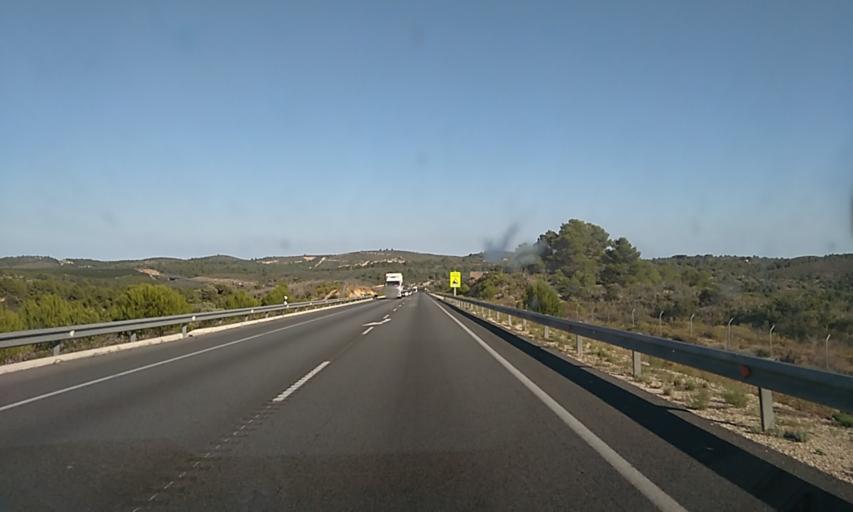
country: ES
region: Valencia
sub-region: Provincia de Castello
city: Torreblanca
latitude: 40.2109
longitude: 0.1293
